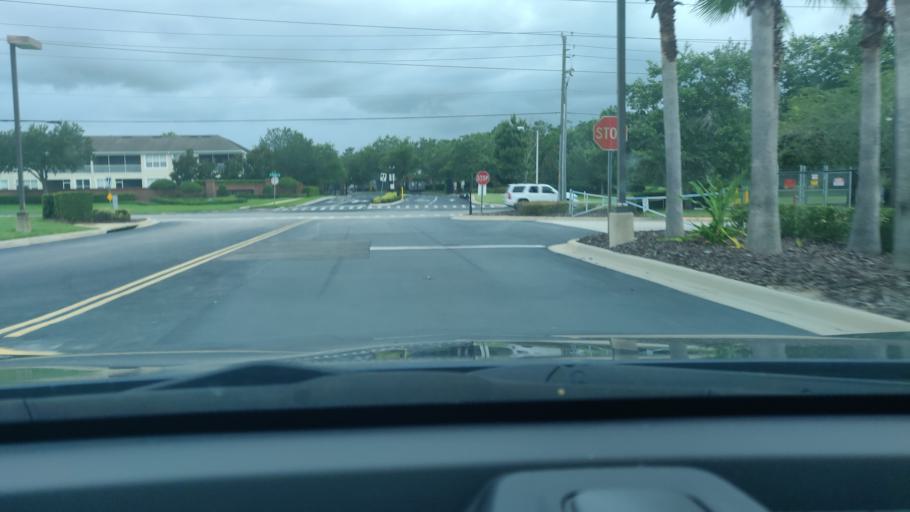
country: US
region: Florida
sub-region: Seminole County
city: Lake Mary
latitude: 28.8153
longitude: -81.3387
